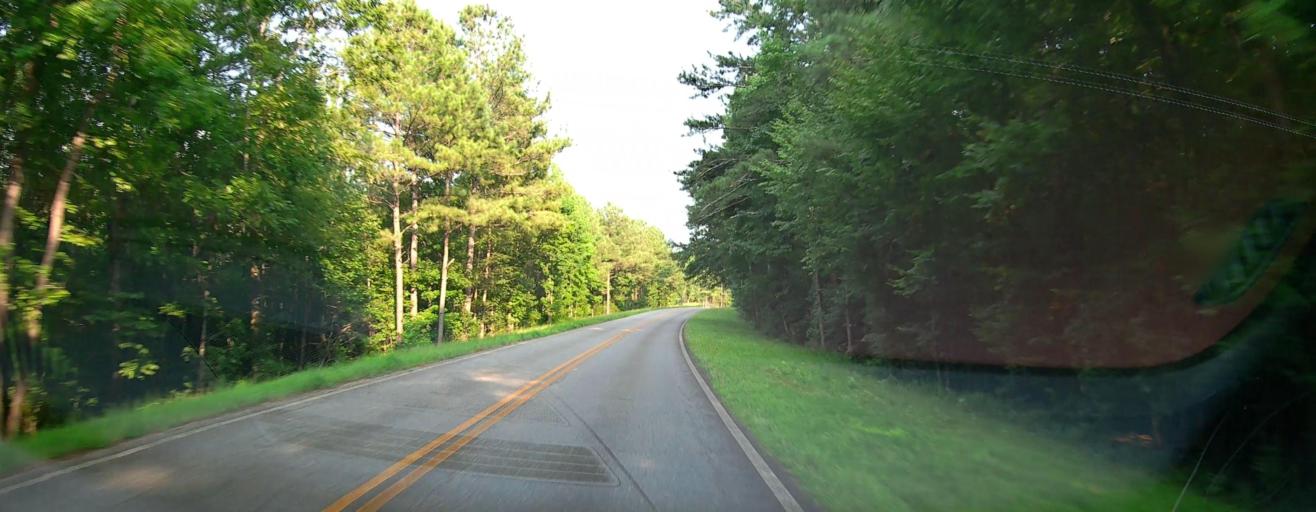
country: US
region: Georgia
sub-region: Monroe County
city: Forsyth
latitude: 33.1088
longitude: -83.7799
